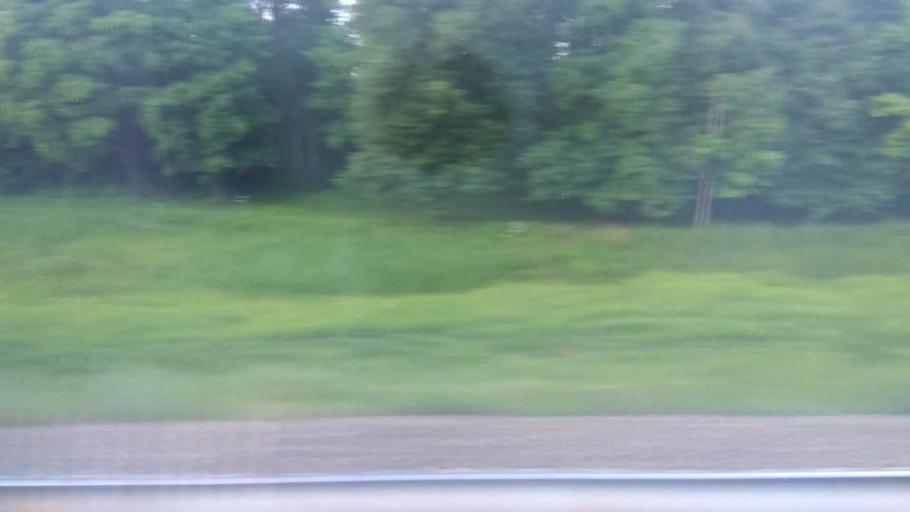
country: RU
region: Moskovskaya
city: Vostryakovo
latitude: 55.3984
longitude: 37.8030
